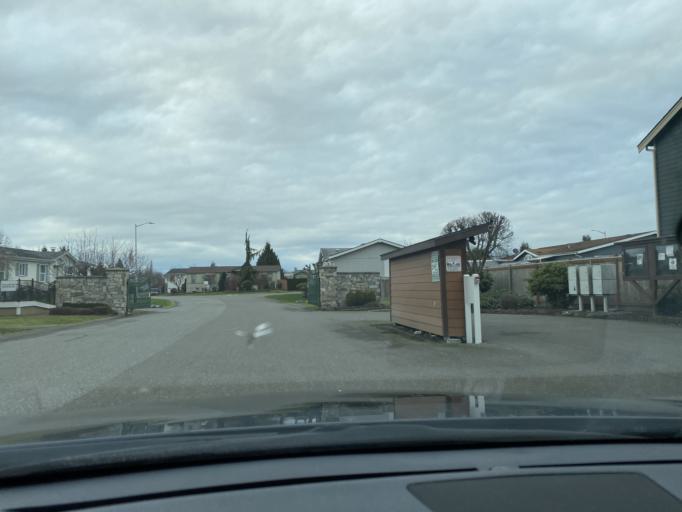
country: US
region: Washington
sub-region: Snohomish County
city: Marysville
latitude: 48.0859
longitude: -122.1520
